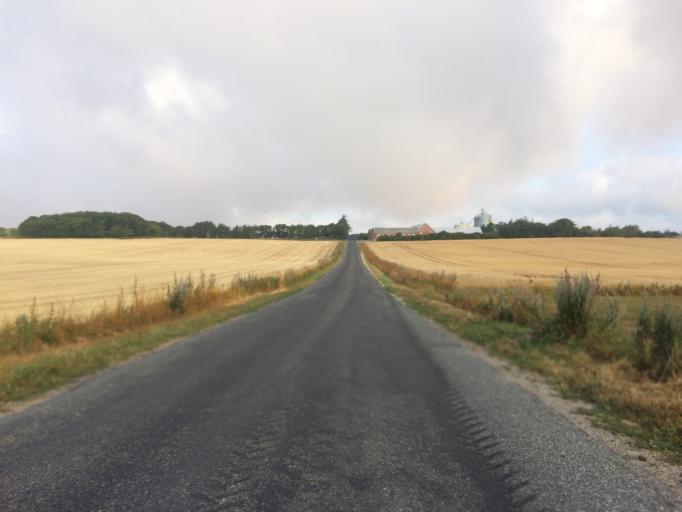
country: DK
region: Central Jutland
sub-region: Holstebro Kommune
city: Vinderup
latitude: 56.5925
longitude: 8.7465
